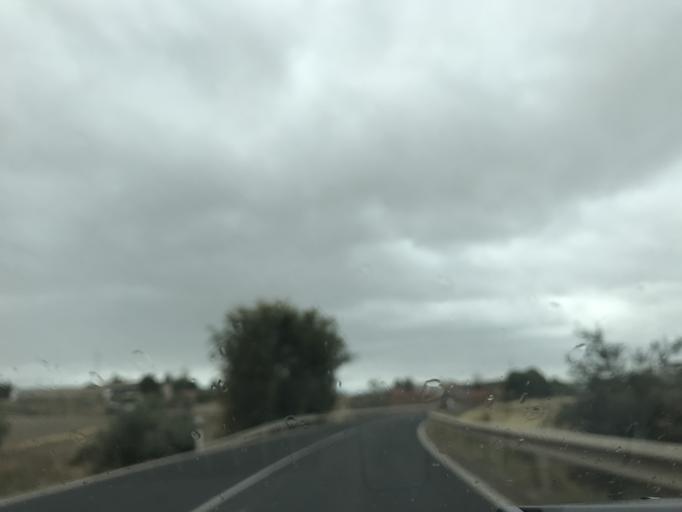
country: ES
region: Andalusia
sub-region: Provincia de Jaen
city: Peal de Becerro
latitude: 37.9178
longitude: -3.1273
